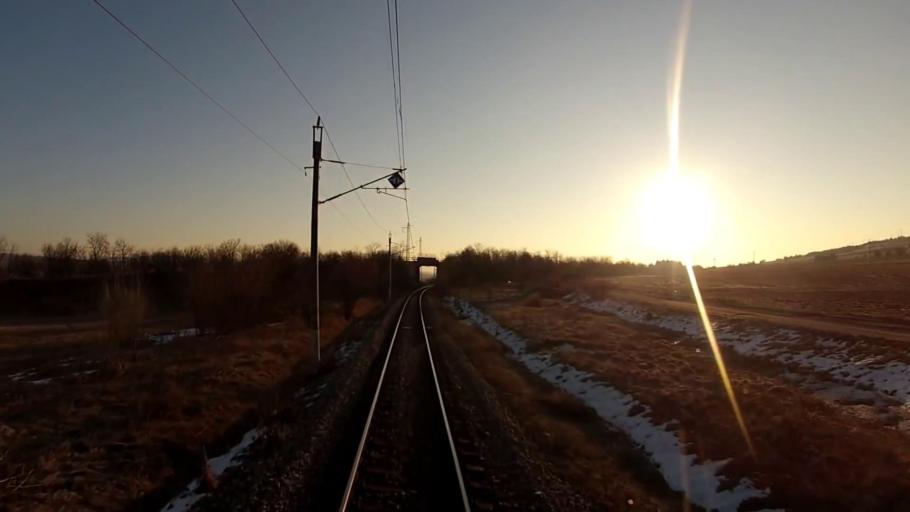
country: BG
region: Sofiya
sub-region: Obshtina Slivnitsa
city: Slivnitsa
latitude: 42.8777
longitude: 23.0171
